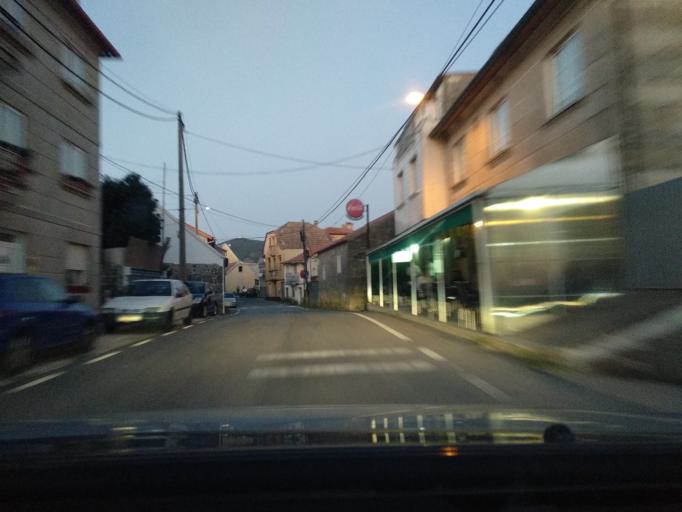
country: ES
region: Galicia
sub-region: Provincia de Pontevedra
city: Moana
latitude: 42.2816
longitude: -8.7447
